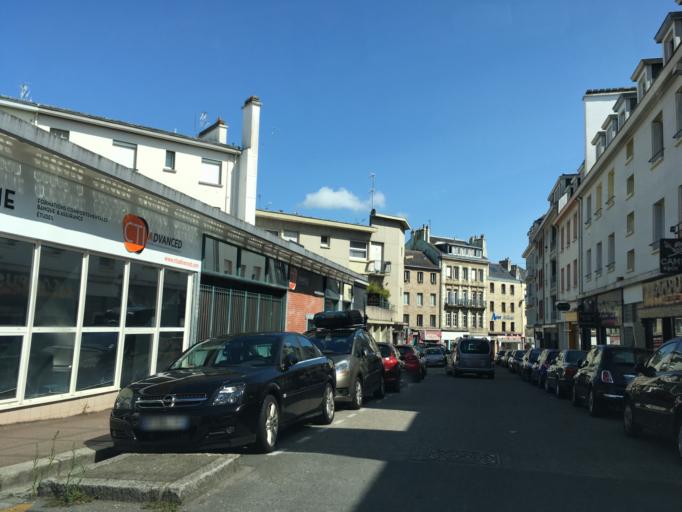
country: FR
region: Brittany
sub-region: Departement du Morbihan
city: Lorient
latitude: 47.7506
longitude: -3.3611
